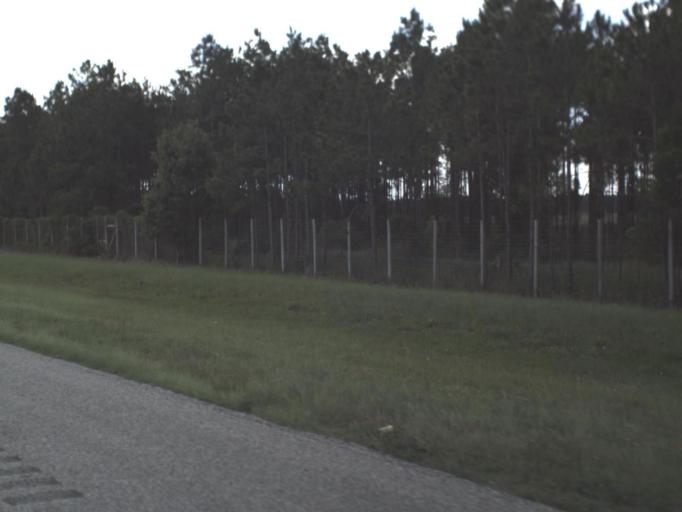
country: US
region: Florida
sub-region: Flagler County
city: Palm Coast
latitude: 29.6682
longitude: -81.2981
